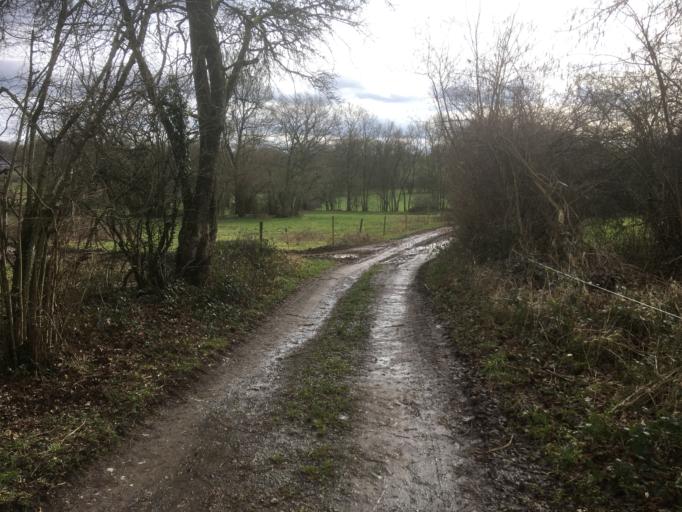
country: BE
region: Wallonia
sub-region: Province du Luxembourg
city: Erezee
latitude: 50.3167
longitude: 5.5059
